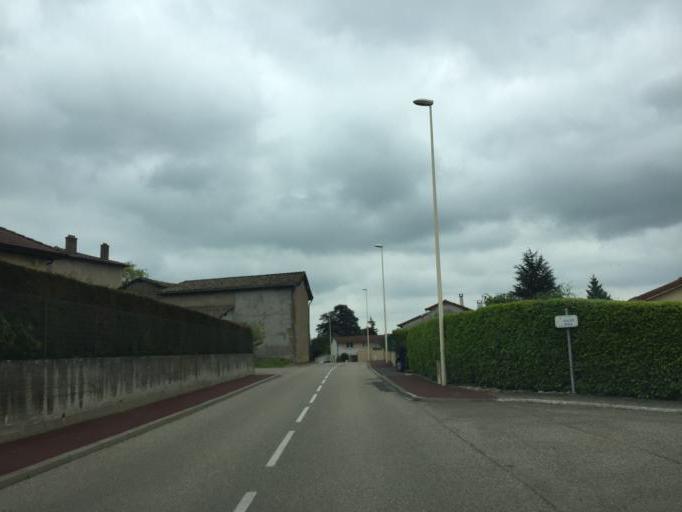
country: FR
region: Rhone-Alpes
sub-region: Departement du Rhone
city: Rillieux-la-Pape
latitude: 45.8220
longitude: 4.9265
